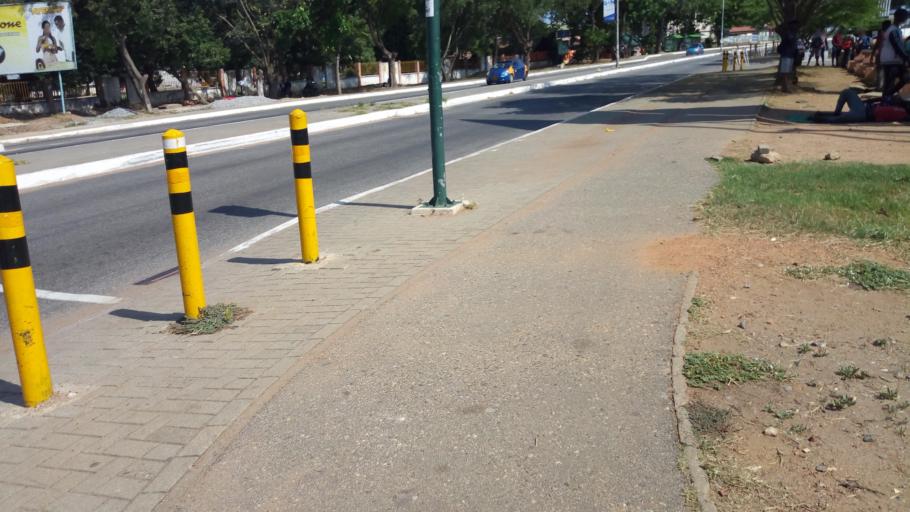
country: GH
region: Greater Accra
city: Accra
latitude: 5.5547
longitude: -0.2007
